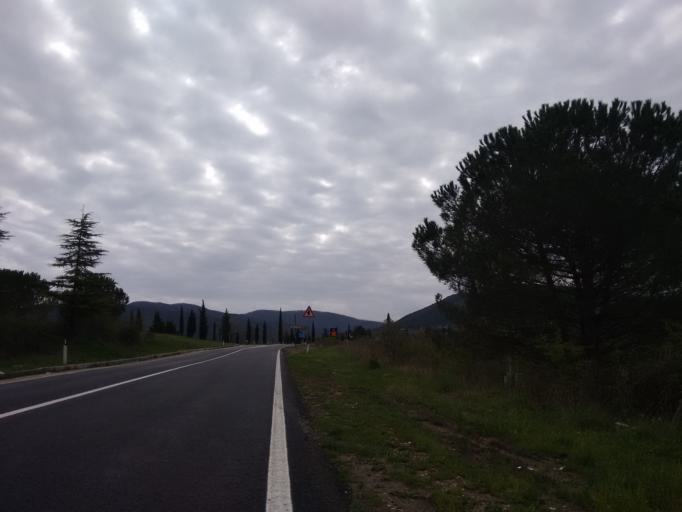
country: IT
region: Tuscany
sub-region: Province of Florence
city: Strada in Chianti
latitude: 43.6527
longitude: 11.3063
